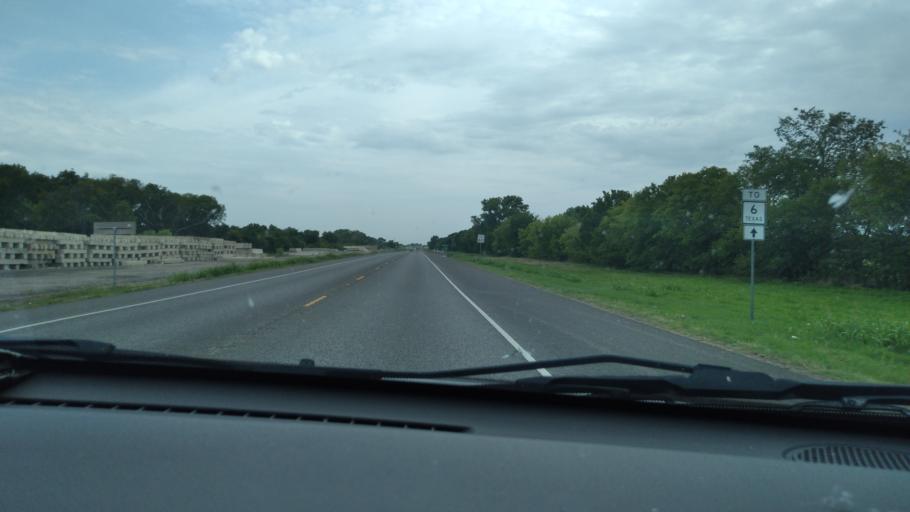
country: US
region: Texas
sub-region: McLennan County
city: Bellmead
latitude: 31.5634
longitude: -97.0676
